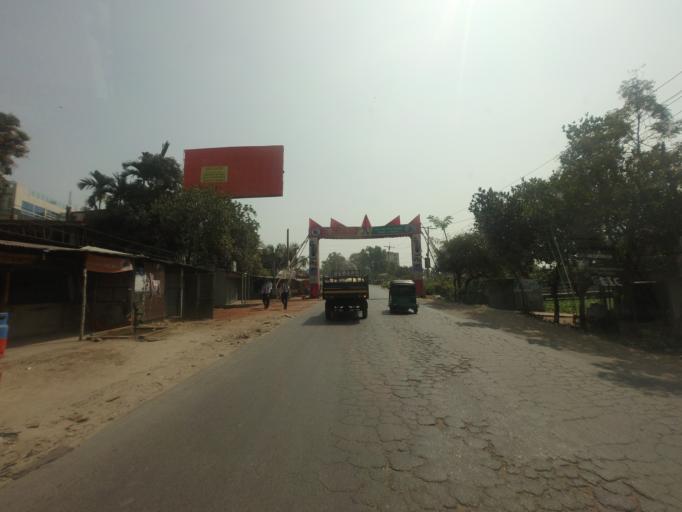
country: BD
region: Dhaka
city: Bhairab Bazar
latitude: 24.0367
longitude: 91.0095
